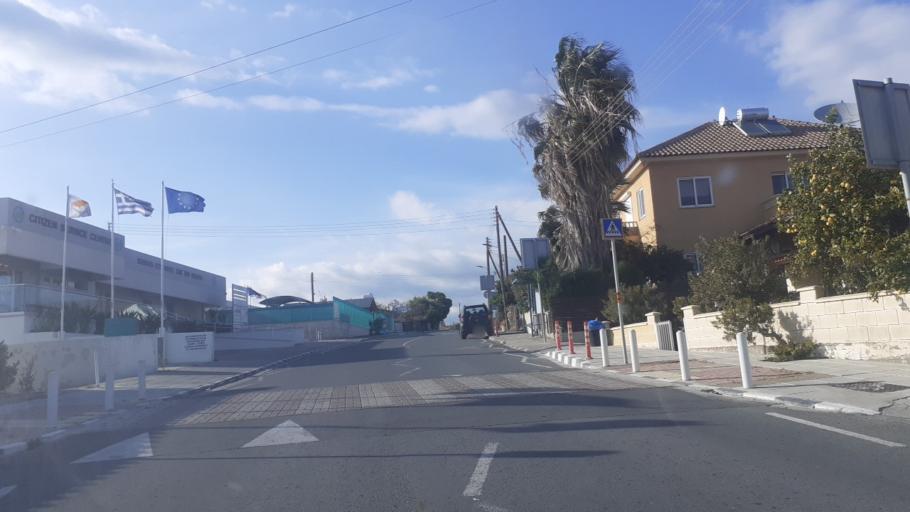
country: CY
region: Larnaka
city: Kolossi
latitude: 34.6827
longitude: 32.9401
